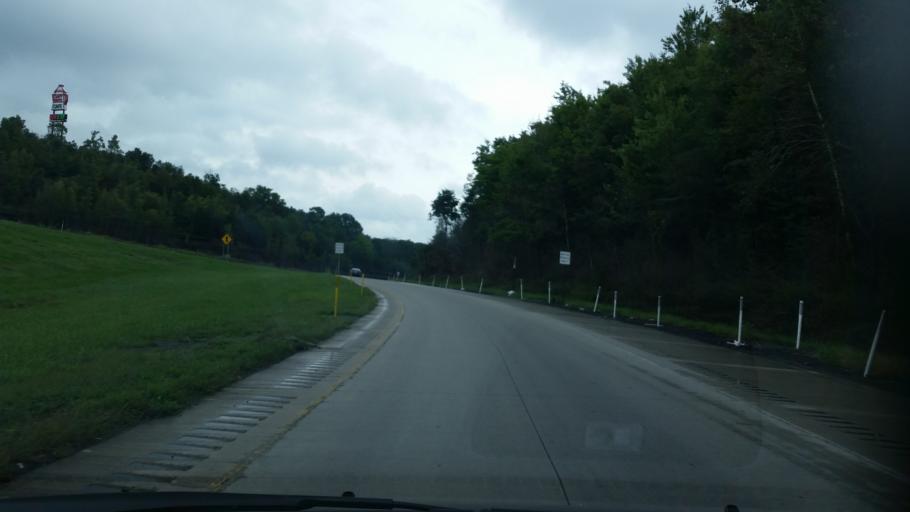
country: US
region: Pennsylvania
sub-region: Clearfield County
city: Clearfield
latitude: 41.0387
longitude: -78.3973
